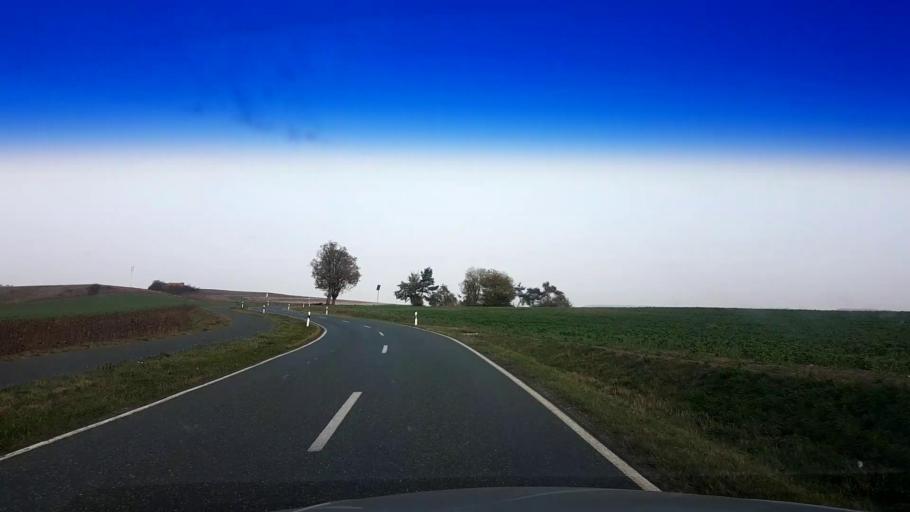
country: DE
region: Bavaria
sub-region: Upper Franconia
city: Altenkunstadt
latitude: 50.1129
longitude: 11.2534
